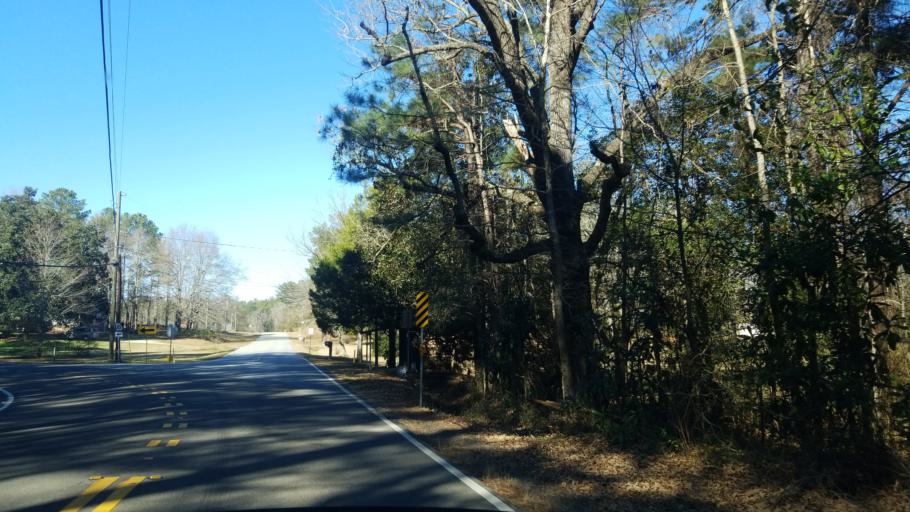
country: US
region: Georgia
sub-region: Harris County
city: Hamilton
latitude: 32.6634
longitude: -84.8680
